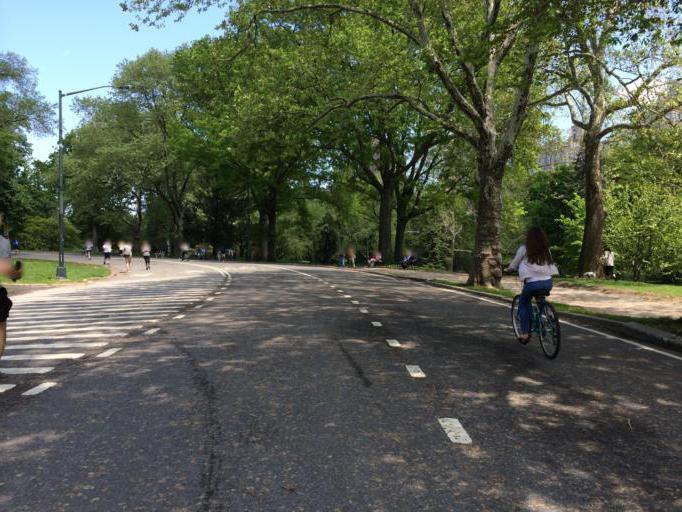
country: US
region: New York
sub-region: New York County
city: Manhattan
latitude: 40.7753
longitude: -73.9678
